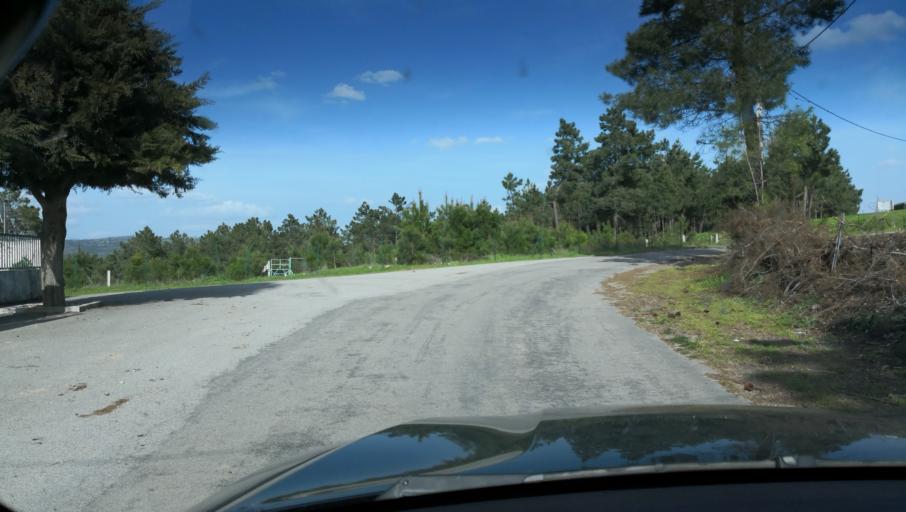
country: PT
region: Vila Real
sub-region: Sabrosa
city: Vilela
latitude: 41.2526
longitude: -7.6589
